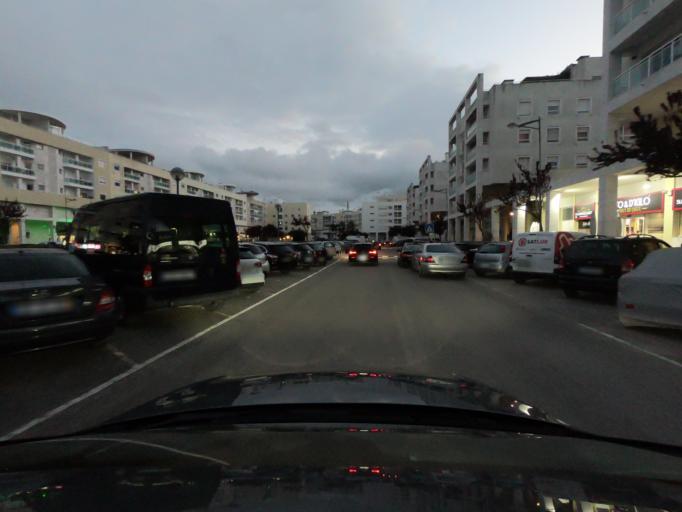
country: PT
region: Lisbon
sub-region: Oeiras
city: Oeiras
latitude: 38.7032
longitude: -9.3059
